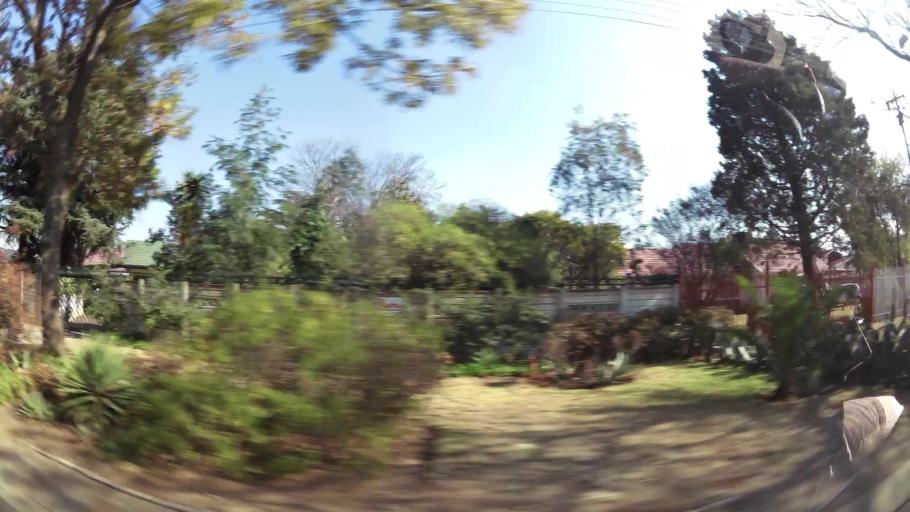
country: ZA
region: Gauteng
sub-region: West Rand District Municipality
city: Randfontein
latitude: -26.1590
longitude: 27.7027
